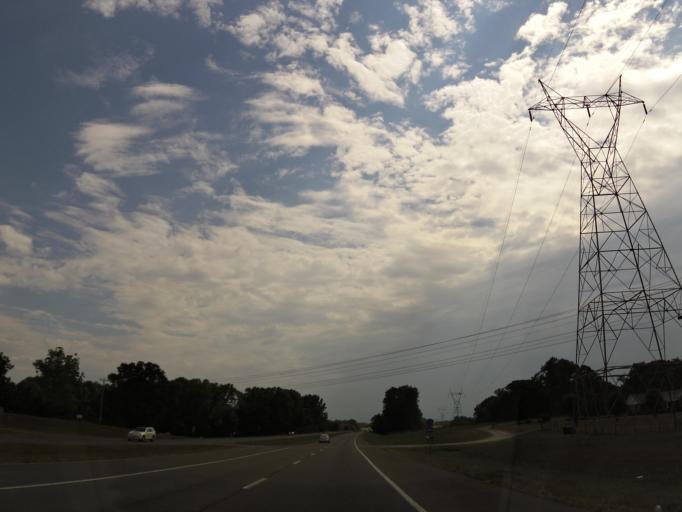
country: US
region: Alabama
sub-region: Jackson County
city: Stevenson
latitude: 34.7709
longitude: -85.8961
